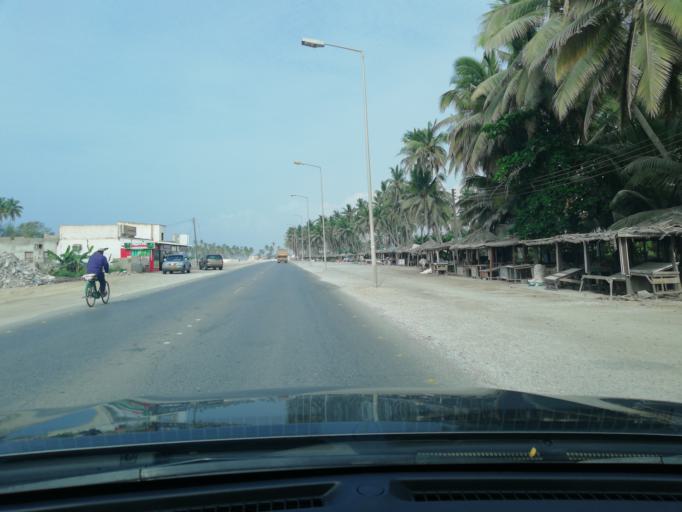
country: OM
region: Zufar
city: Salalah
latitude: 17.0039
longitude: 54.1170
